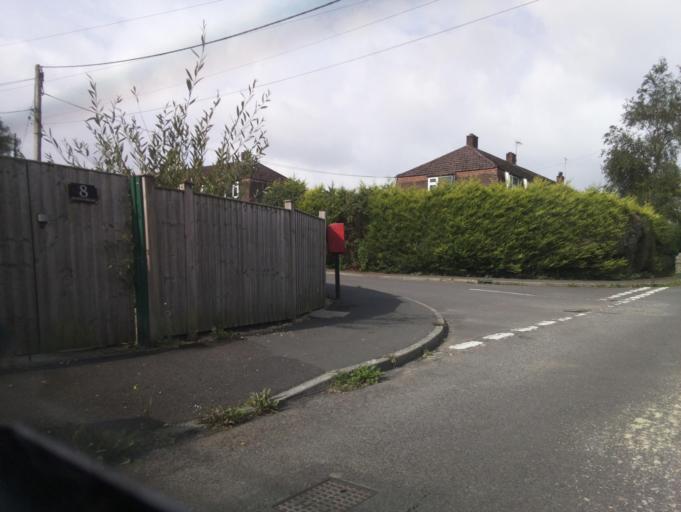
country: GB
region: England
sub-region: Somerset
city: Shepton Mallet
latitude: 51.2241
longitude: -2.5329
